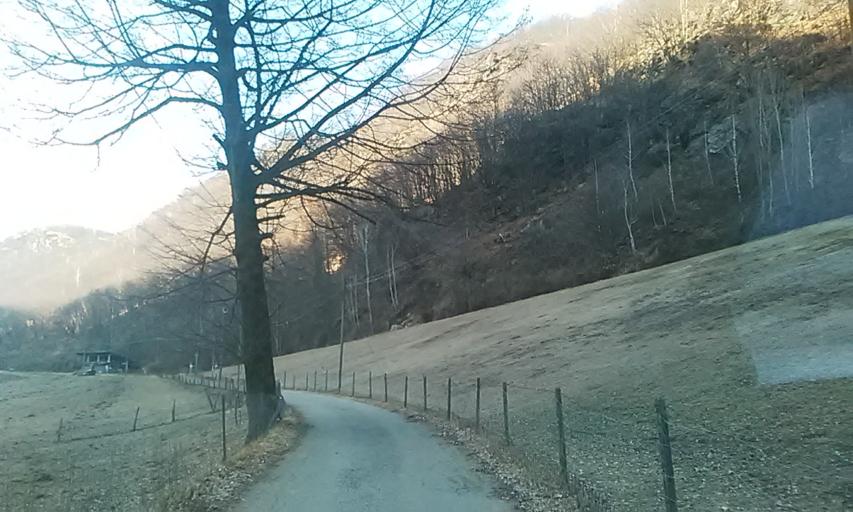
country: IT
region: Piedmont
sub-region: Provincia di Vercelli
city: Quarona
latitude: 45.7745
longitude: 8.2761
